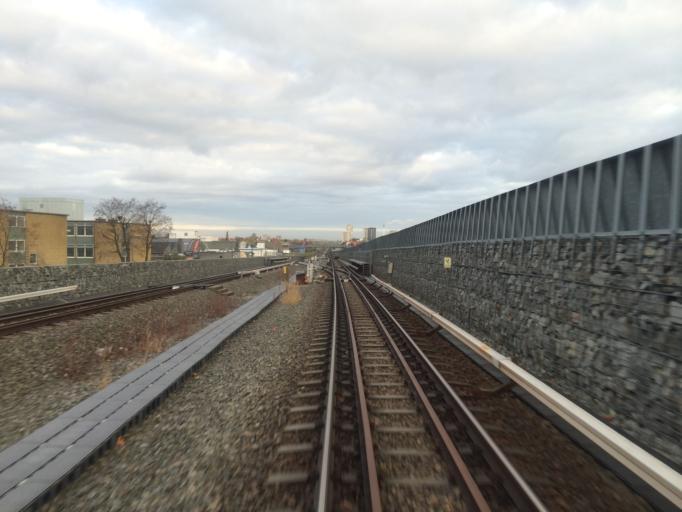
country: DK
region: Capital Region
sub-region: Tarnby Kommune
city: Tarnby
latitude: 55.6458
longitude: 12.6378
